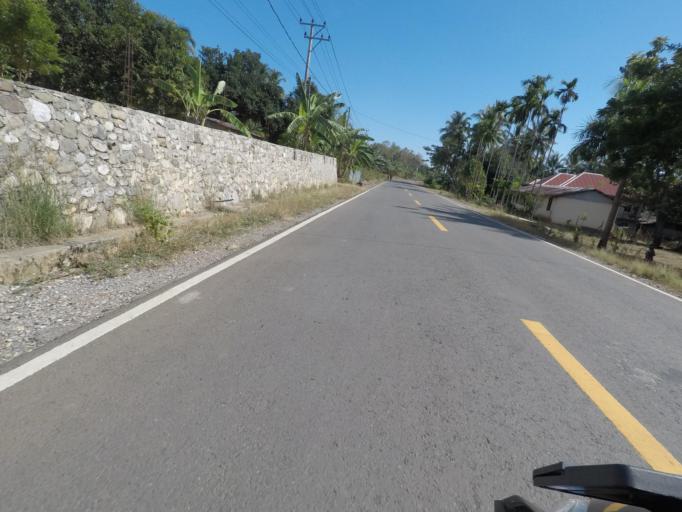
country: TL
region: Bobonaro
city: Maliana
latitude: -8.9579
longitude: 125.2136
